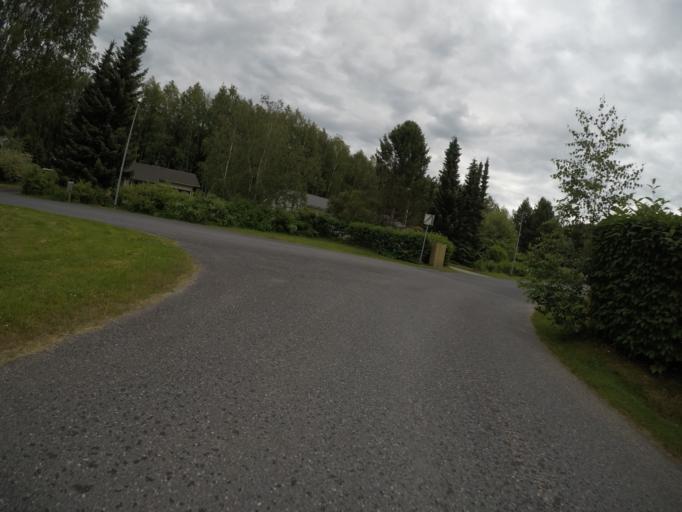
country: FI
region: Haeme
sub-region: Haemeenlinna
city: Haemeenlinna
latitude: 60.9768
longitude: 24.4677
